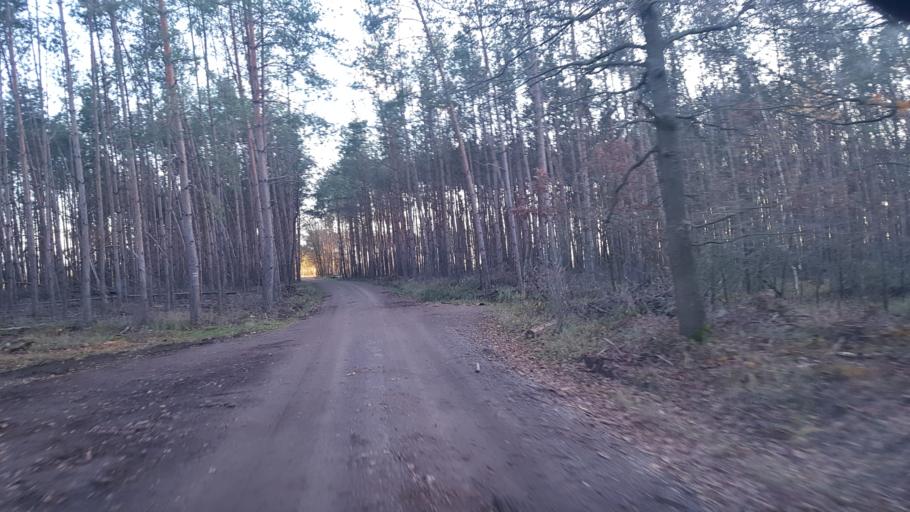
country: DE
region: Brandenburg
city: Falkenberg
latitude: 51.6147
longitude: 13.2825
